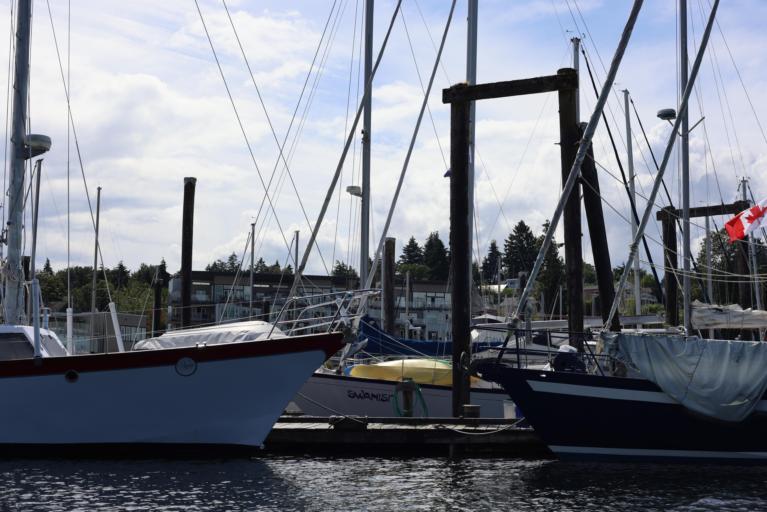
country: CA
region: British Columbia
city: Nanaimo
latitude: 49.1849
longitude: -123.9446
